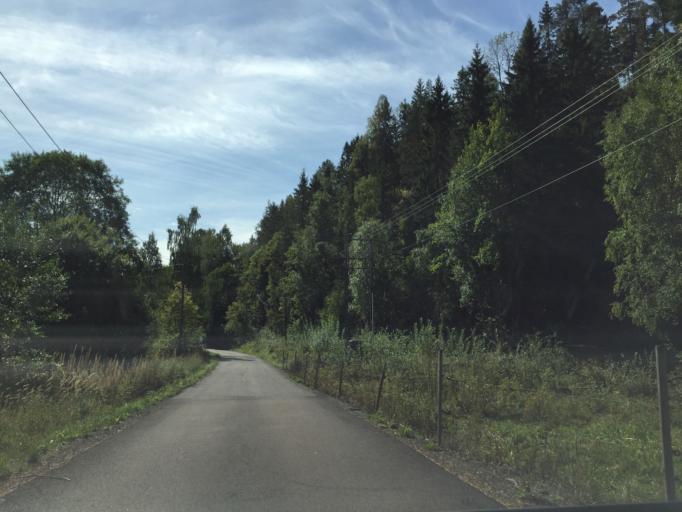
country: NO
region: Vestfold
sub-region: Hof
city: Hof
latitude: 59.4693
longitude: 10.1444
